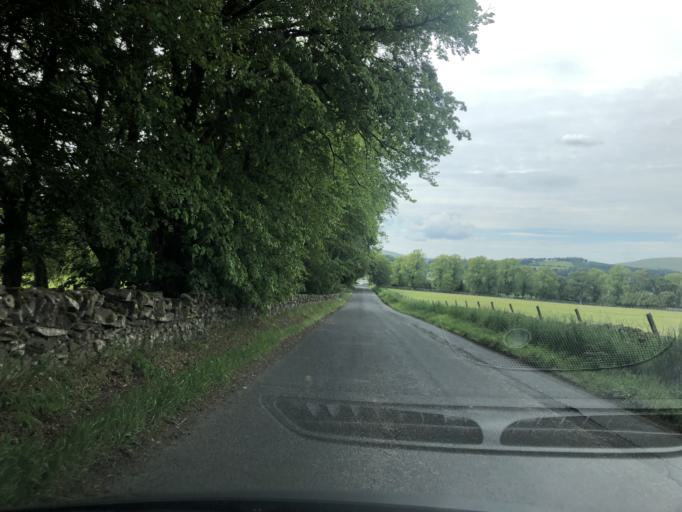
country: GB
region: Scotland
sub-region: The Scottish Borders
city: West Linton
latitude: 55.7423
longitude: -3.3423
